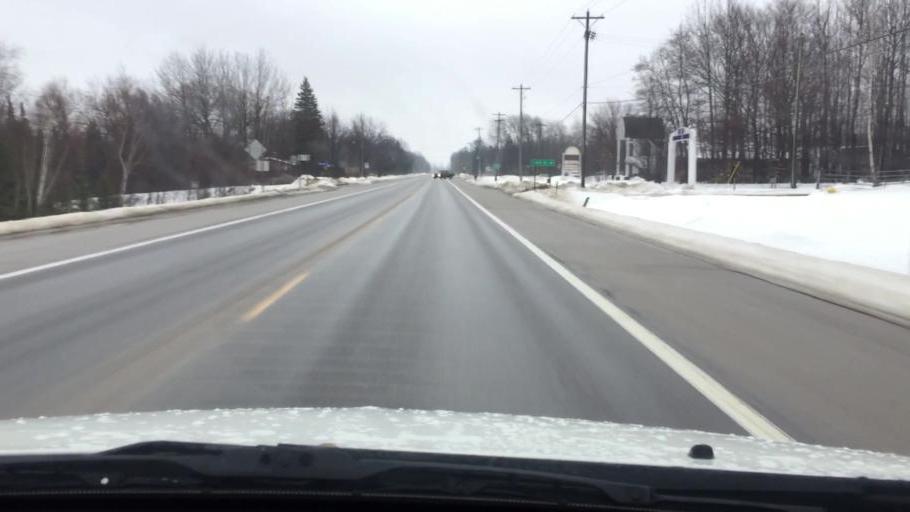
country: US
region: Michigan
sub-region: Charlevoix County
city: Charlevoix
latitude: 45.2939
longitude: -85.2517
